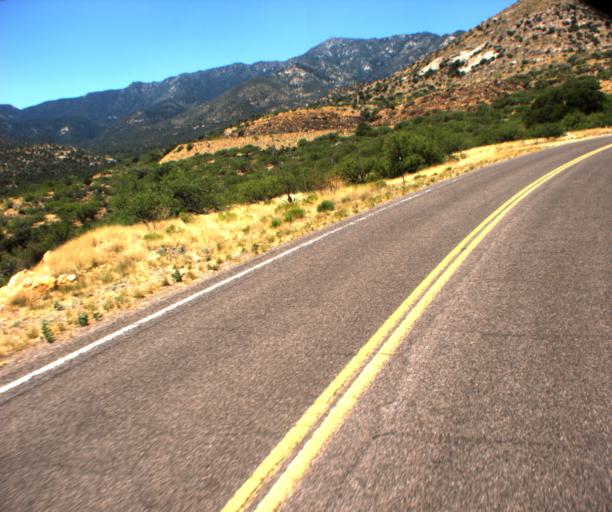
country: US
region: Arizona
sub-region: Graham County
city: Swift Trail Junction
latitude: 32.6788
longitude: -109.7735
